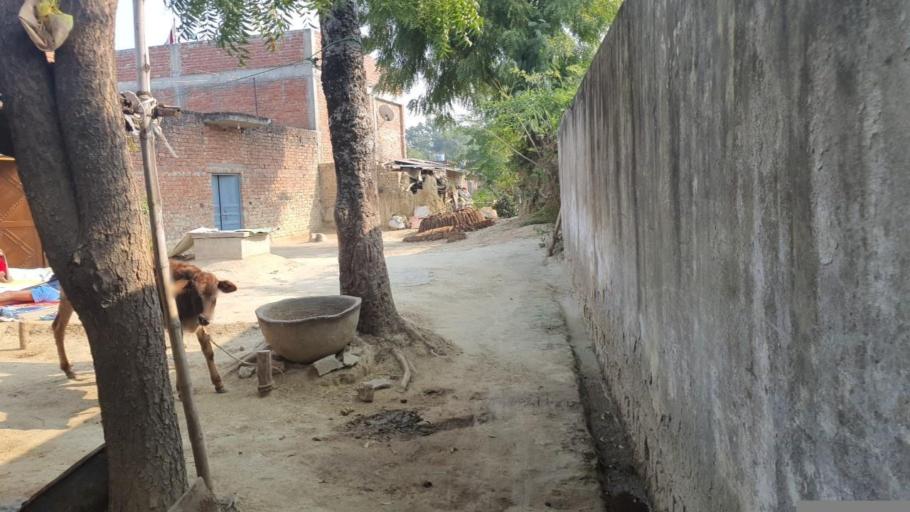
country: IN
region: Uttar Pradesh
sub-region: Lucknow District
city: Lucknow
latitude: 26.7959
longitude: 81.0088
